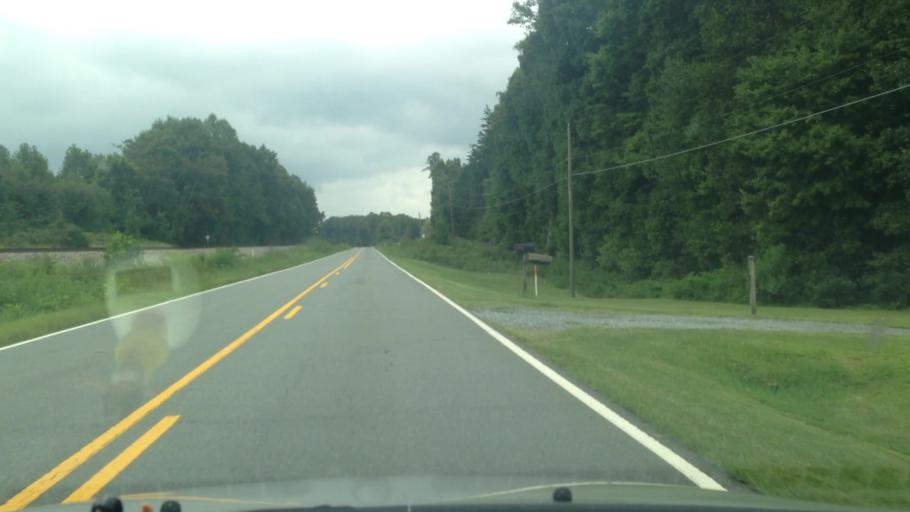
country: US
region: North Carolina
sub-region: Stokes County
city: Walnut Cove
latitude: 36.2532
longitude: -80.1492
